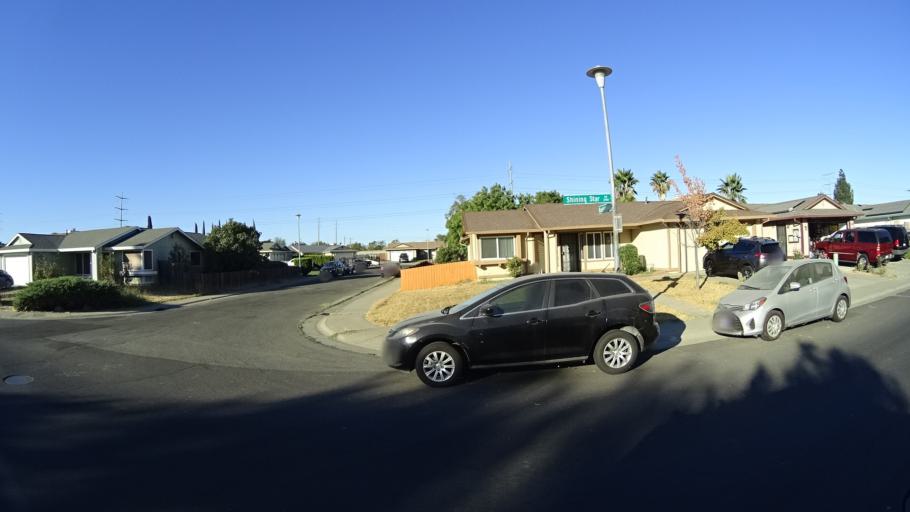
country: US
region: California
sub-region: Sacramento County
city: Parkway
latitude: 38.4849
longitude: -121.4656
